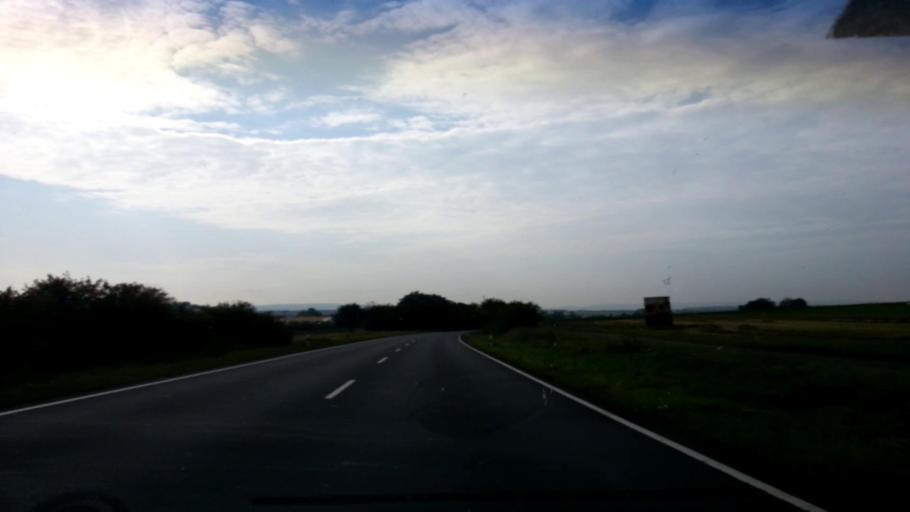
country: DE
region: Bavaria
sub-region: Regierungsbezirk Unterfranken
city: Lulsfeld
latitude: 49.8533
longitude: 10.3522
